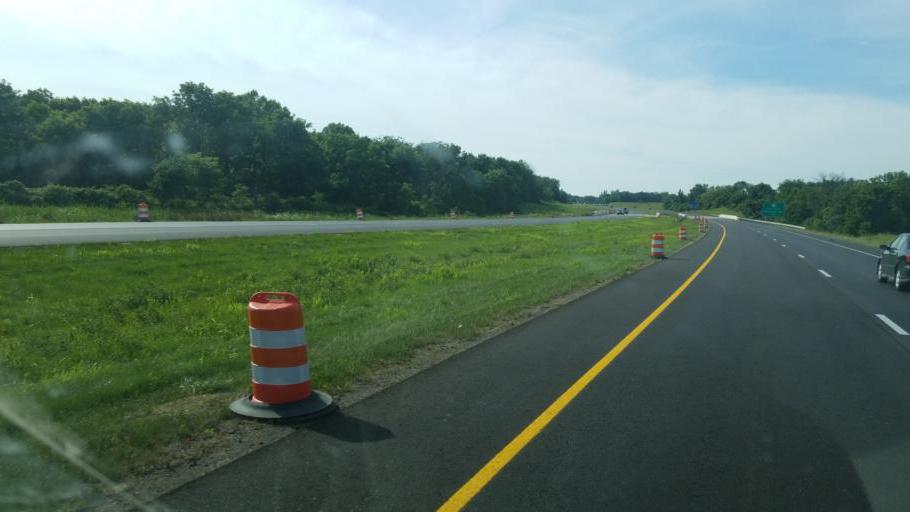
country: US
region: Ohio
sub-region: Fairfield County
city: Lancaster
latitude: 39.7566
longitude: -82.6791
